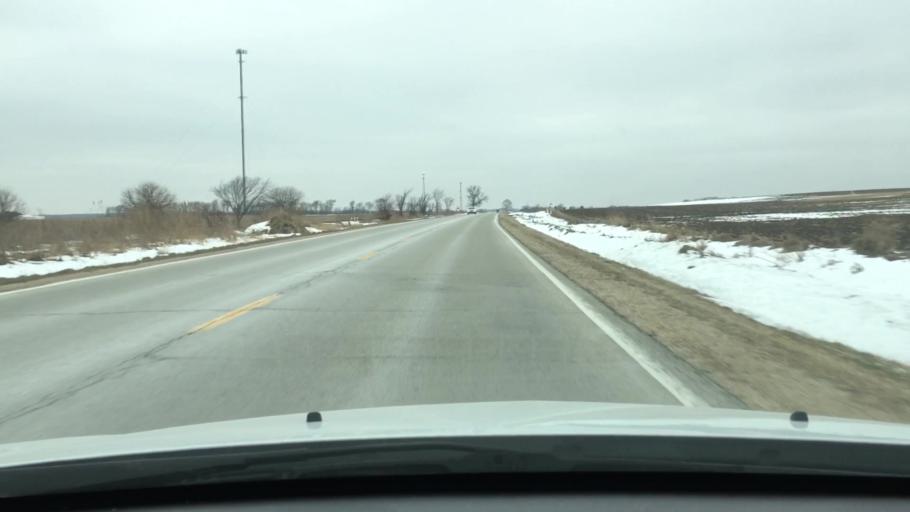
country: US
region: Illinois
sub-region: DeKalb County
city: Waterman
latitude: 41.7694
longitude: -88.8008
